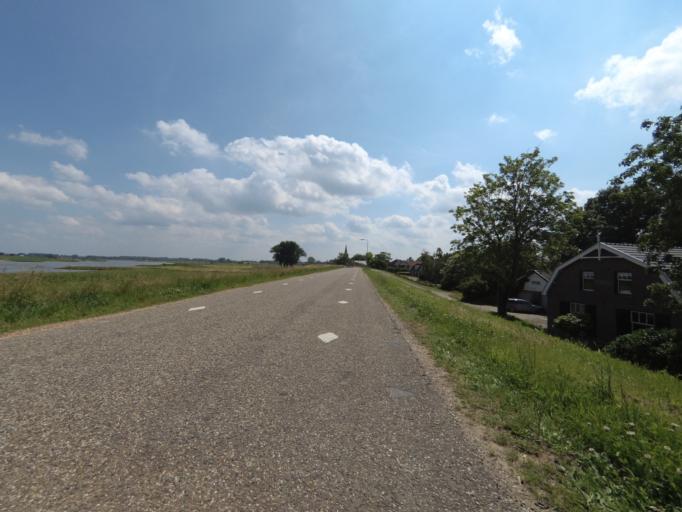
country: NL
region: Utrecht
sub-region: Gemeente Wijk bij Duurstede
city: Wijk bij Duurstede
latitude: 51.9534
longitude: 5.3231
